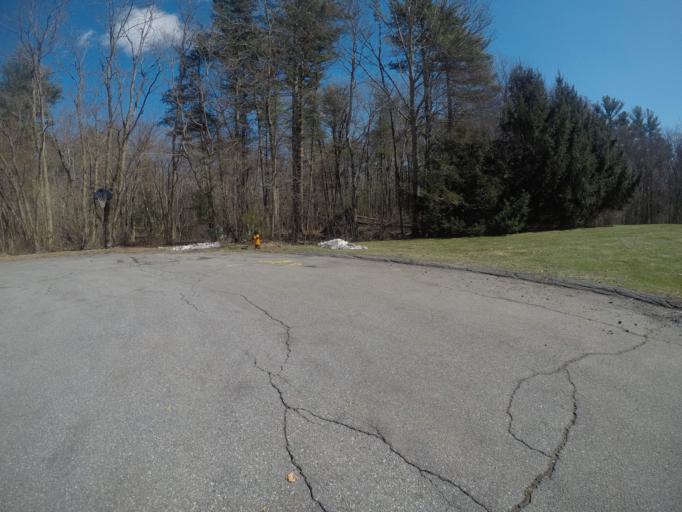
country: US
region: Massachusetts
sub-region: Bristol County
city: Easton
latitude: 42.0076
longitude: -71.1006
